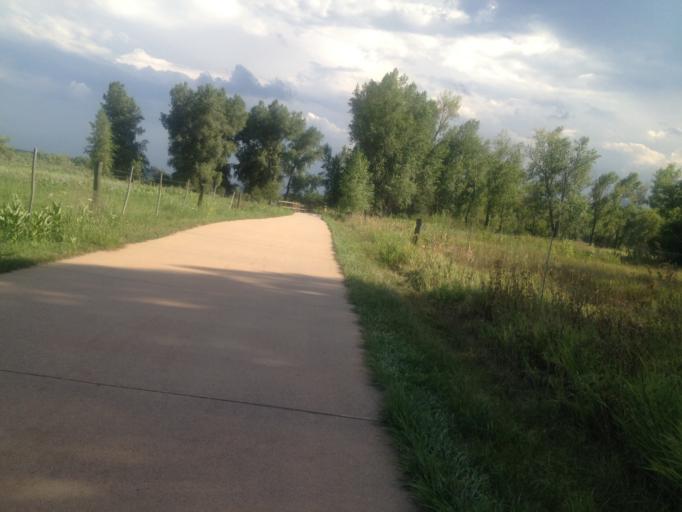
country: US
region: Colorado
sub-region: Boulder County
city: Boulder
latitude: 39.9984
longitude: -105.2147
